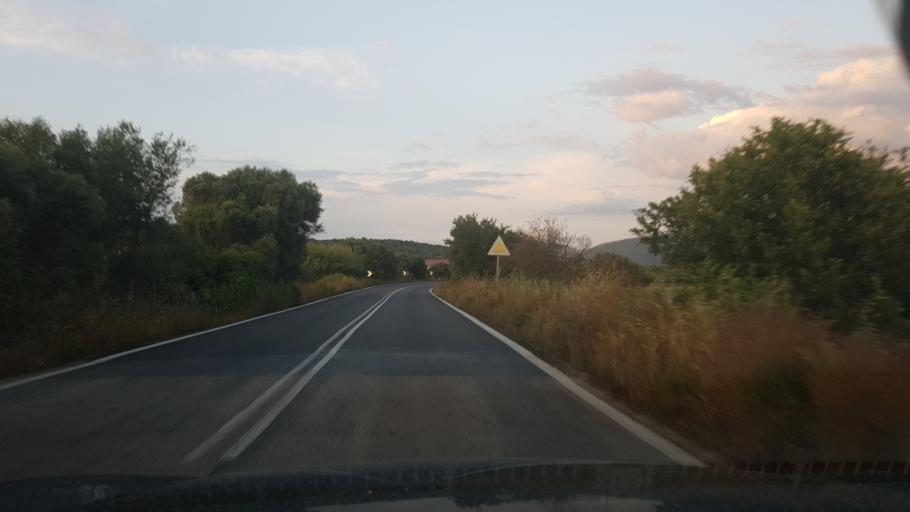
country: GR
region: West Greece
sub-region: Nomos Aitolias kai Akarnanias
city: Vonitsa
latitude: 38.8815
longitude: 20.8289
